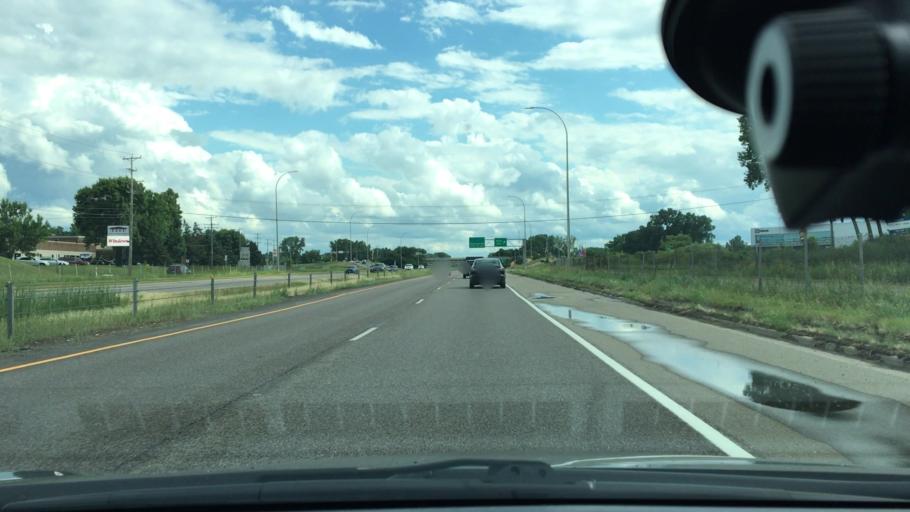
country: US
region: Minnesota
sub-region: Hennepin County
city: New Hope
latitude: 45.0485
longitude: -93.4010
